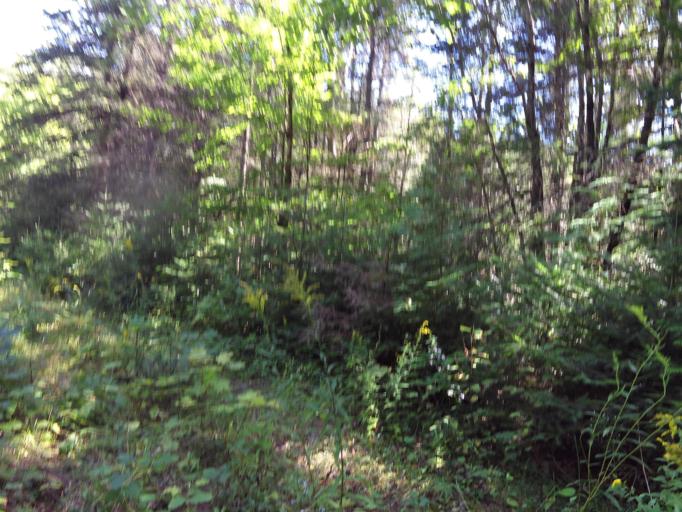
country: CA
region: Ontario
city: Renfrew
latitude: 45.0261
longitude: -76.6970
